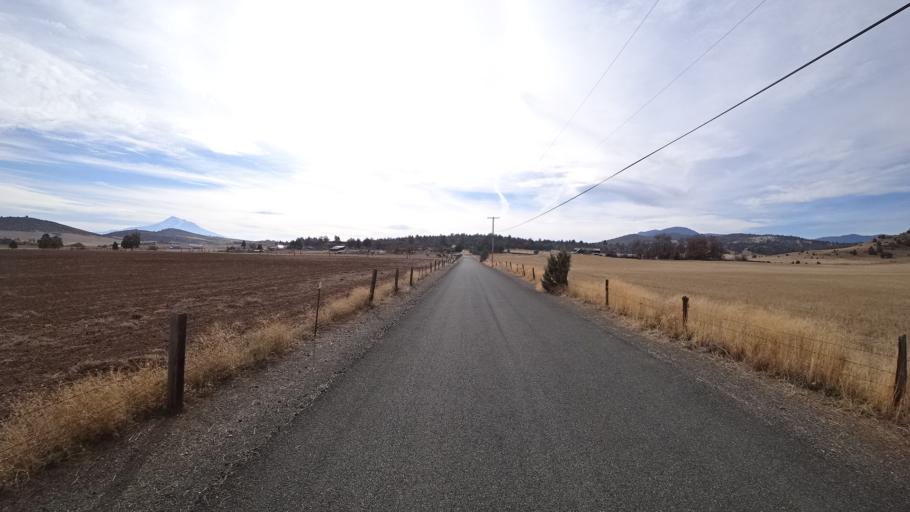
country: US
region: California
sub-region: Siskiyou County
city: Montague
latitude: 41.6967
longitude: -122.5639
